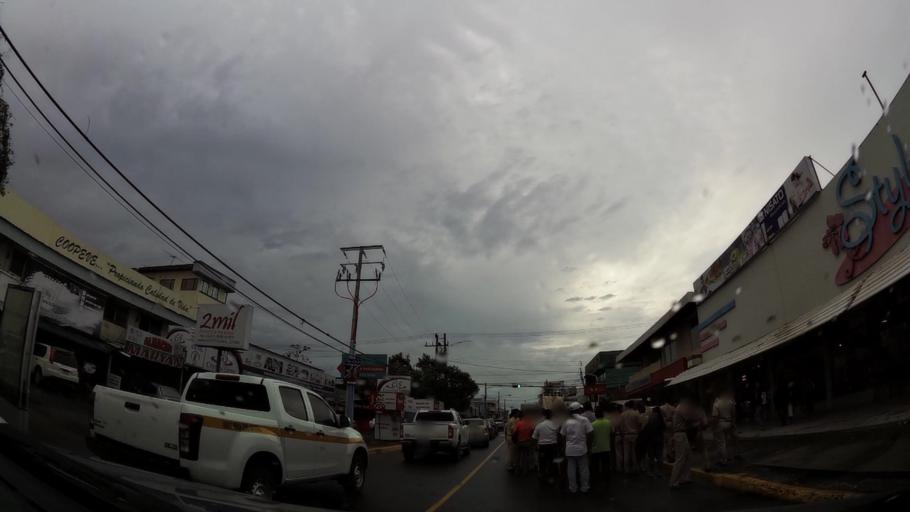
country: PA
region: Veraguas
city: Santiago de Veraguas
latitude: 8.0973
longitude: -80.9798
